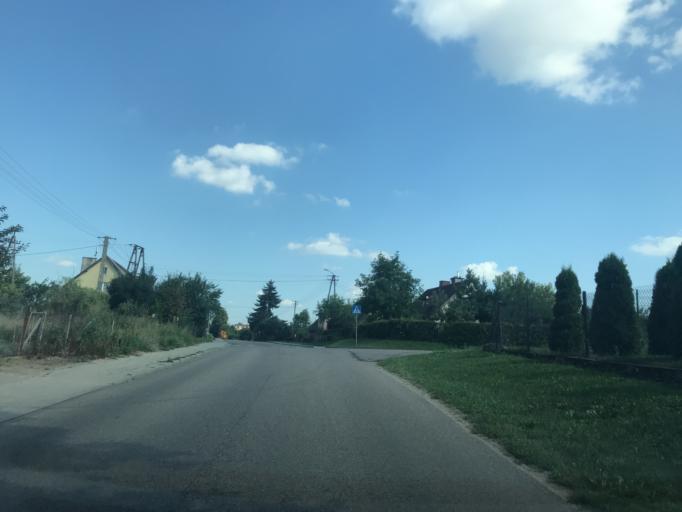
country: PL
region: Masovian Voivodeship
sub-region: Powiat mlawski
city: Mlawa
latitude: 53.1102
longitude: 20.3403
